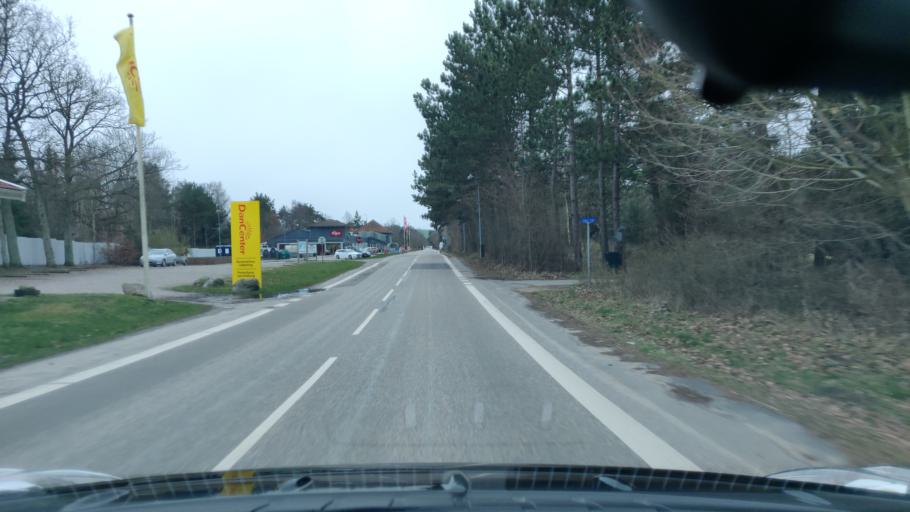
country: DK
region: Zealand
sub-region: Odsherred Kommune
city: Asnaes
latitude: 55.8598
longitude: 11.5281
